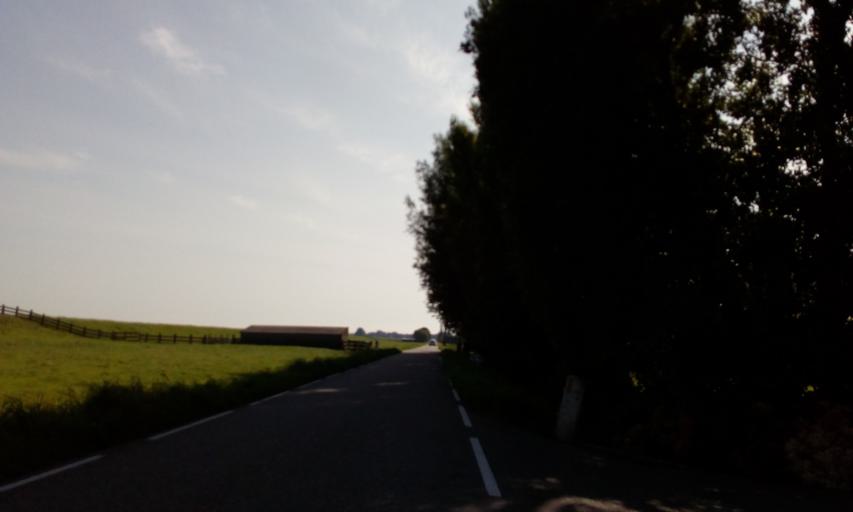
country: NL
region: South Holland
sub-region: Gemeente Waddinxveen
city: Groenswaard
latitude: 52.0477
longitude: 4.6166
